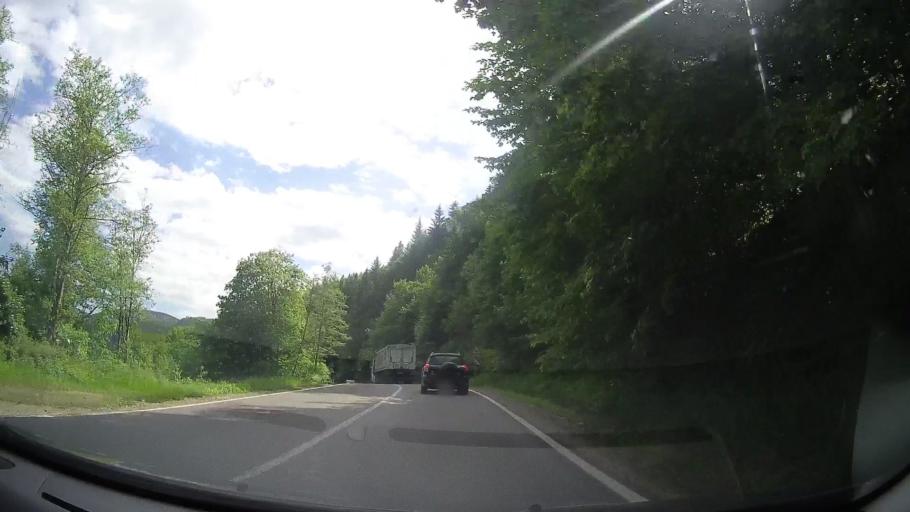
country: RO
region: Prahova
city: Maneciu
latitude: 45.3767
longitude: 25.9293
